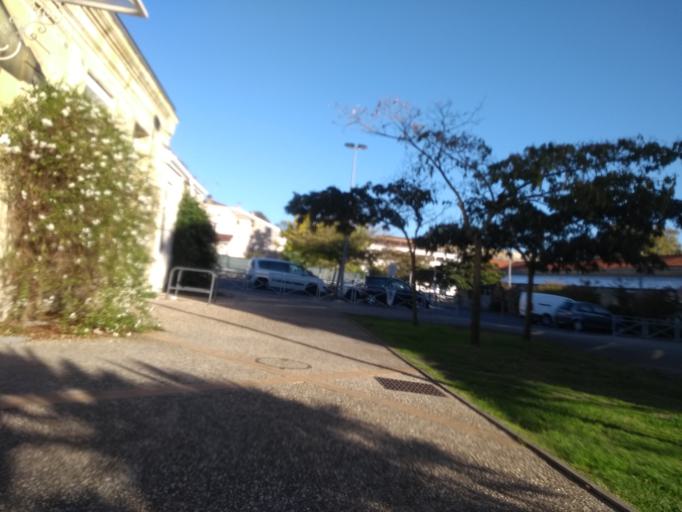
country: FR
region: Aquitaine
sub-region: Departement de la Gironde
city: Talence
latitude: 44.8104
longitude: -0.5894
